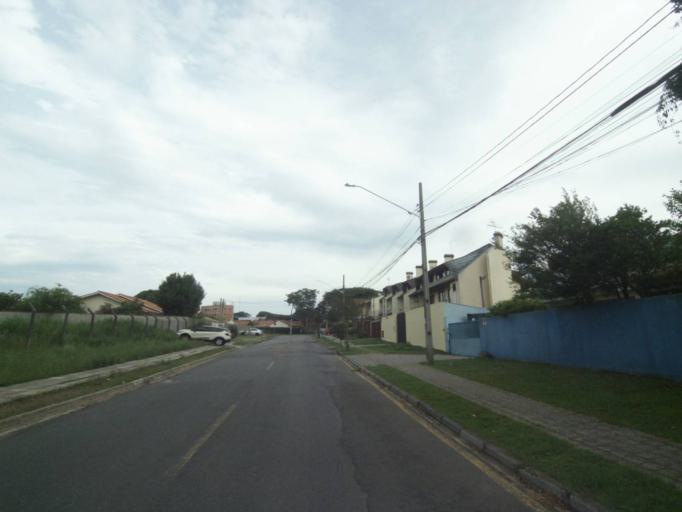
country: BR
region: Parana
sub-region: Curitiba
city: Curitiba
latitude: -25.4258
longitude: -49.2307
